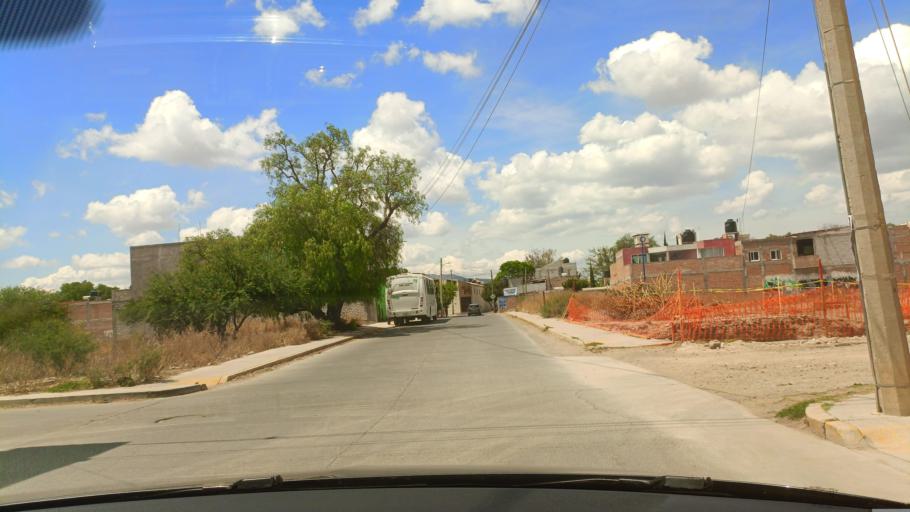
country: MX
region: Guanajuato
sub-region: San Luis de la Paz
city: San Luis de la Paz
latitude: 21.3035
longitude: -100.5216
